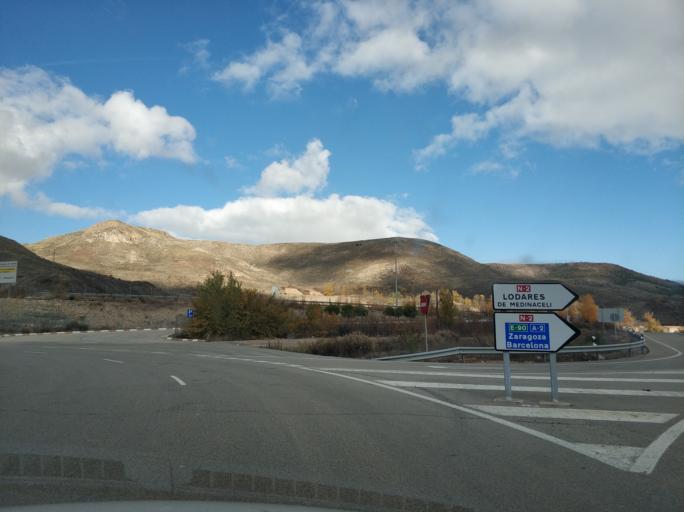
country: ES
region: Castille and Leon
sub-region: Provincia de Soria
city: Medinaceli
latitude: 41.1712
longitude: -2.4186
